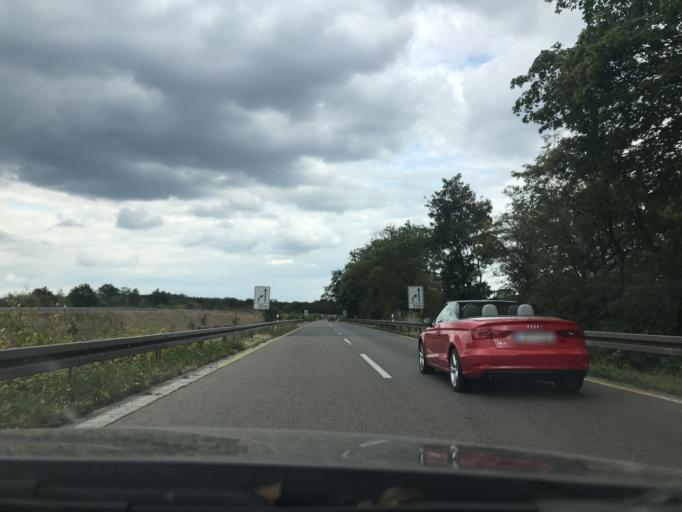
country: DE
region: North Rhine-Westphalia
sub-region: Regierungsbezirk Dusseldorf
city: Erkrath
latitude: 51.1893
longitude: 6.8670
